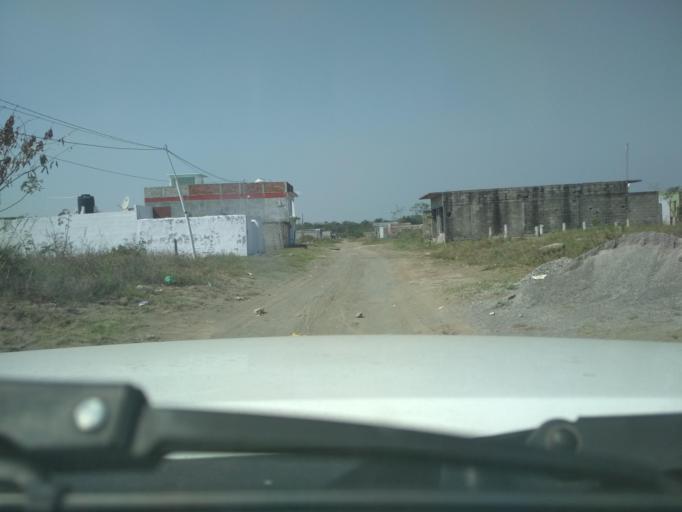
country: MX
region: Veracruz
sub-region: Veracruz
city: Lomas de Rio Medio Cuatro
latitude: 19.1955
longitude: -96.1964
